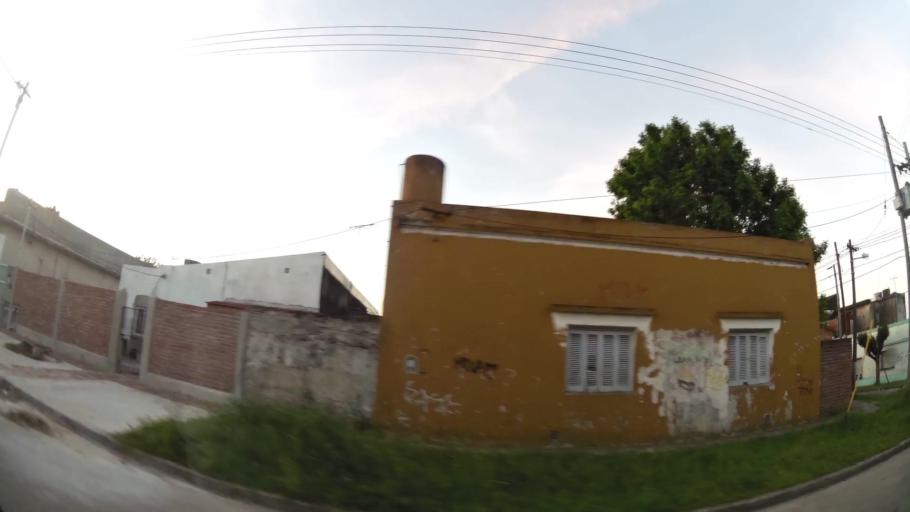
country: AR
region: Buenos Aires
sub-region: Partido de Quilmes
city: Quilmes
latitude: -34.7729
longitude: -58.1994
